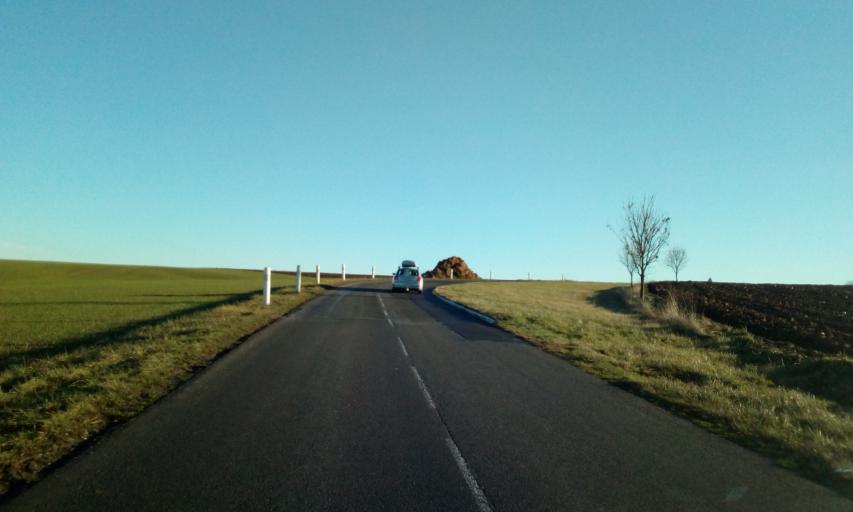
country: FR
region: Picardie
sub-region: Departement de l'Aisne
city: Rozoy-sur-Serre
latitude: 49.7014
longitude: 4.1593
